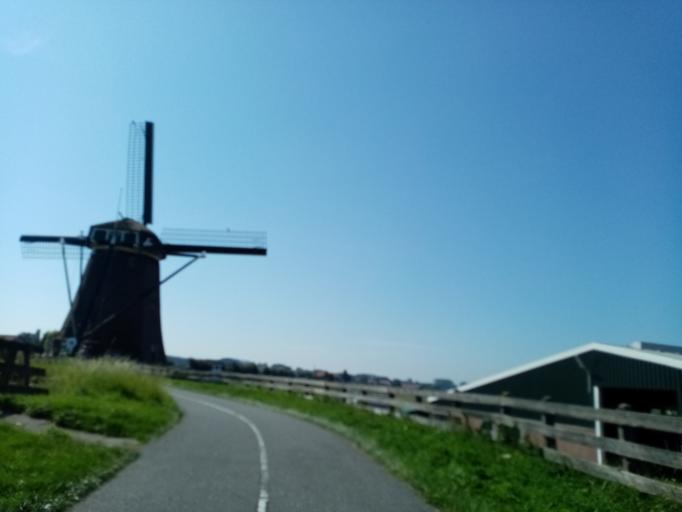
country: NL
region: South Holland
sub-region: Gemeente Lisse
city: Lisse
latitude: 52.2308
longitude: 4.5527
